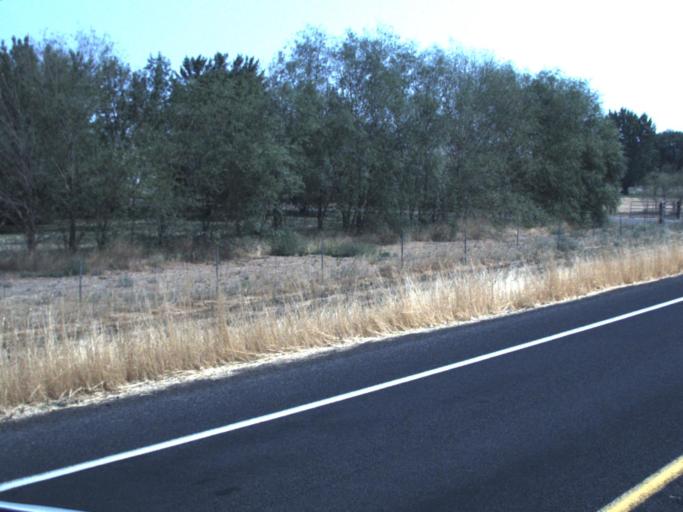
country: US
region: Washington
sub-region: Yakima County
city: Zillah
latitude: 46.5058
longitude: -120.1867
